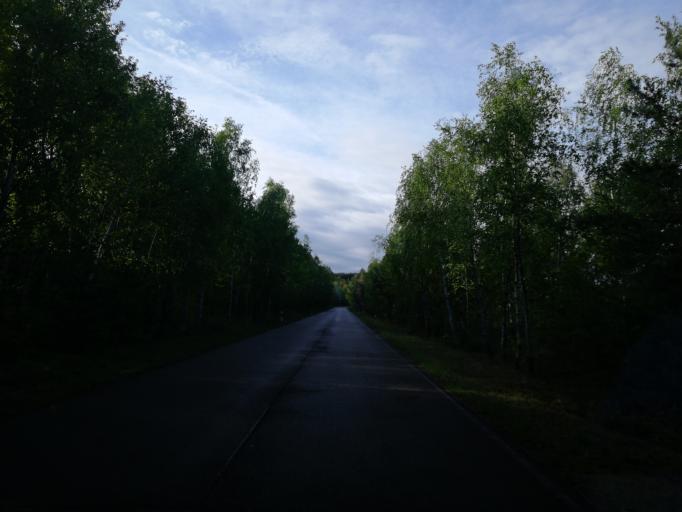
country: DE
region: Brandenburg
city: Lauchhammer
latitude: 51.5277
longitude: 13.7709
